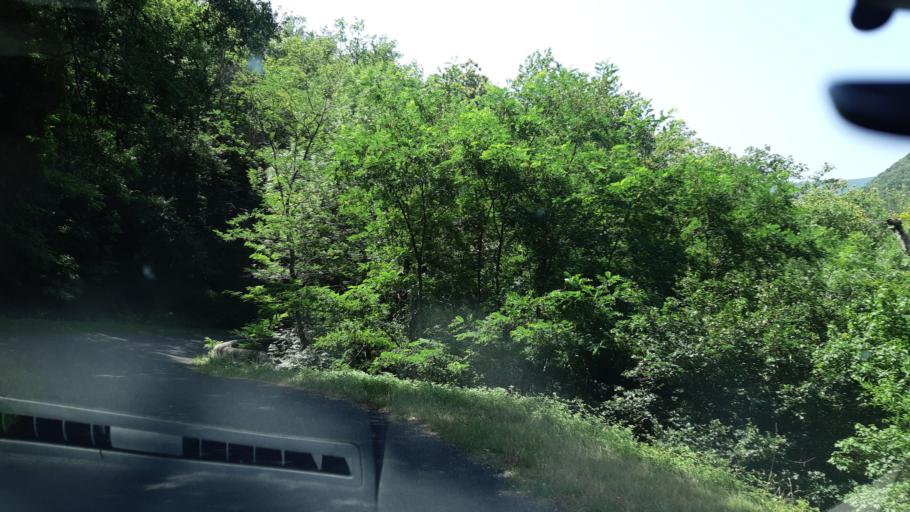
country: FR
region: Languedoc-Roussillon
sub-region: Departement des Pyrenees-Orientales
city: Arles
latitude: 42.5249
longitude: 2.6195
